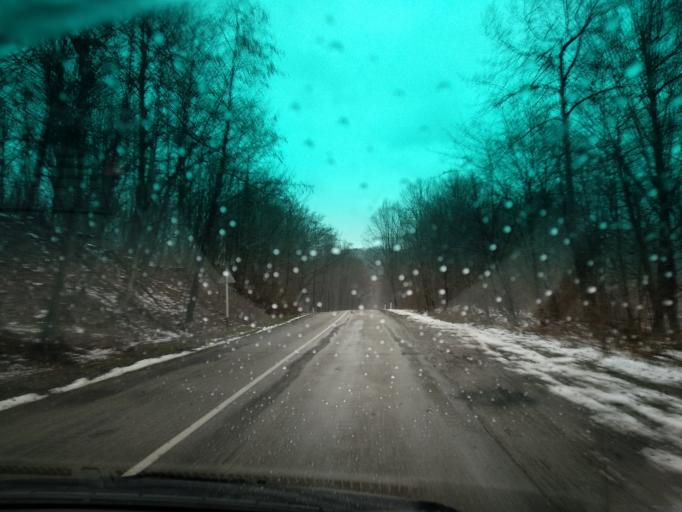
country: RU
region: Krasnodarskiy
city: Khadyzhensk
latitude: 44.2290
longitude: 39.3835
